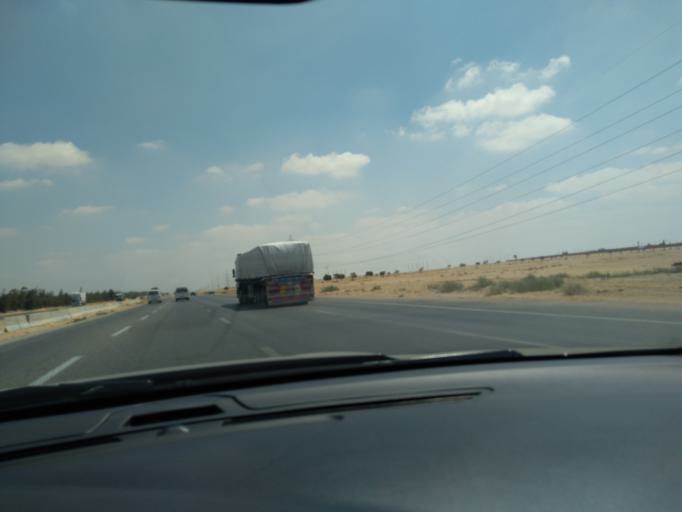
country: EG
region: Al Isma'iliyah
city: At Tall al Kabir
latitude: 30.3906
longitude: 31.9658
